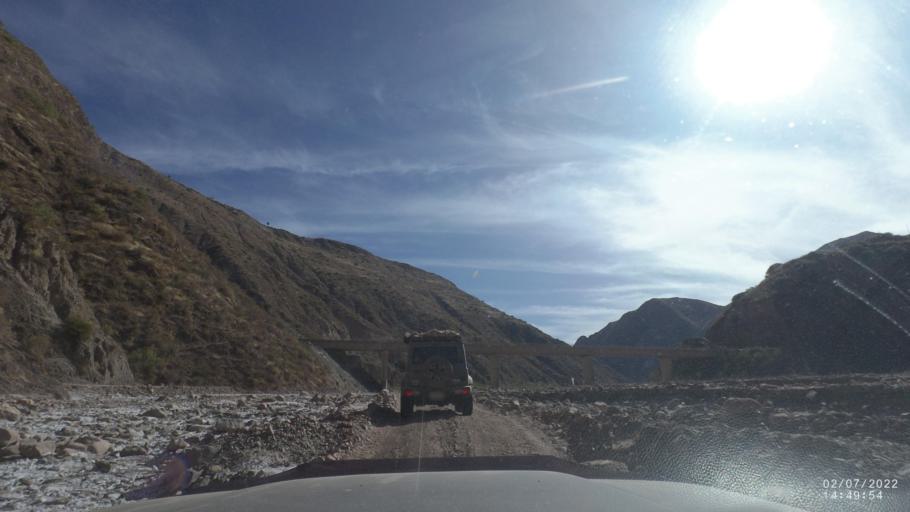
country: BO
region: Cochabamba
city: Irpa Irpa
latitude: -17.8551
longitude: -66.4298
